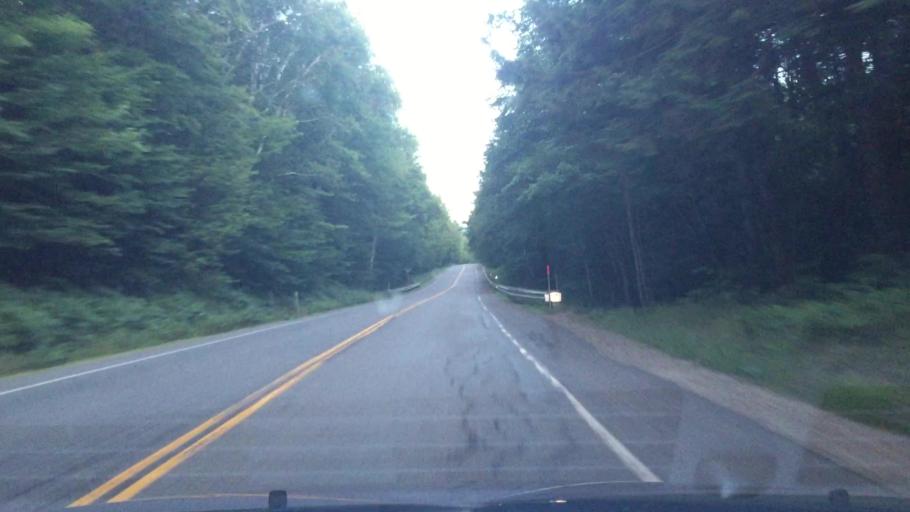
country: US
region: New Hampshire
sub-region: Grafton County
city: Woodstock
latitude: 44.0526
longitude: -71.5731
